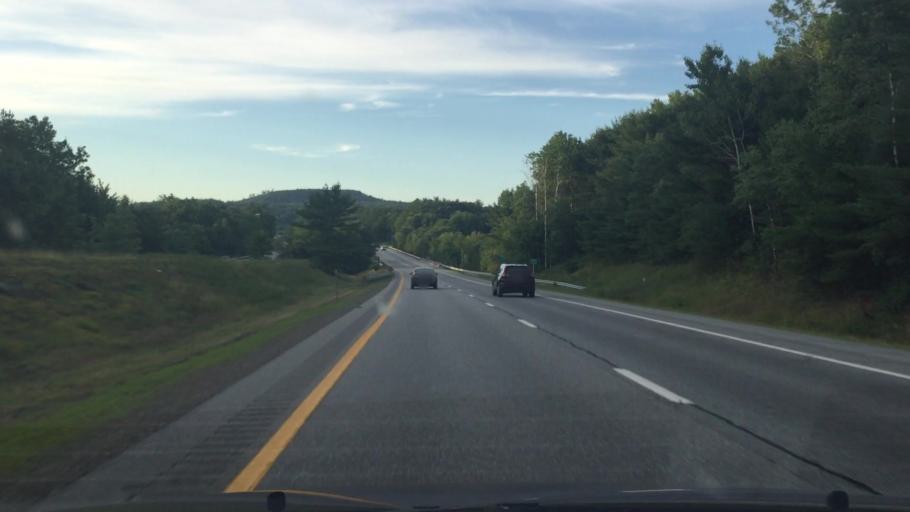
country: US
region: New Hampshire
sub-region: Grafton County
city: Ashland
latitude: 43.6843
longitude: -71.6424
